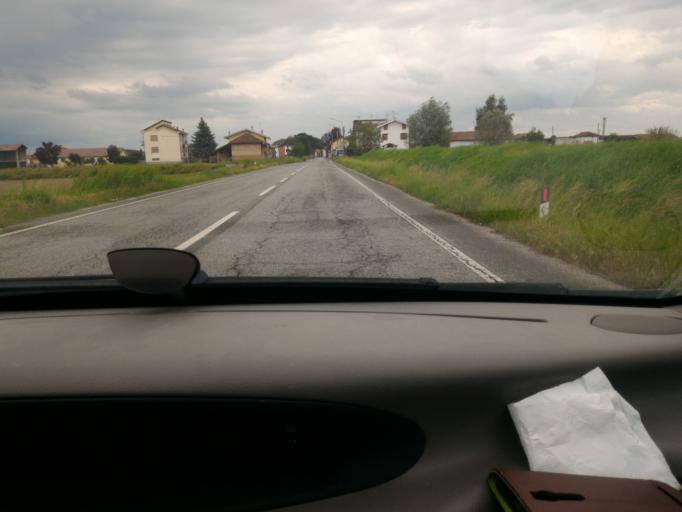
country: IT
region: Piedmont
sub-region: Provincia di Cuneo
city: Villanova Solaro
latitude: 44.7265
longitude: 7.5677
